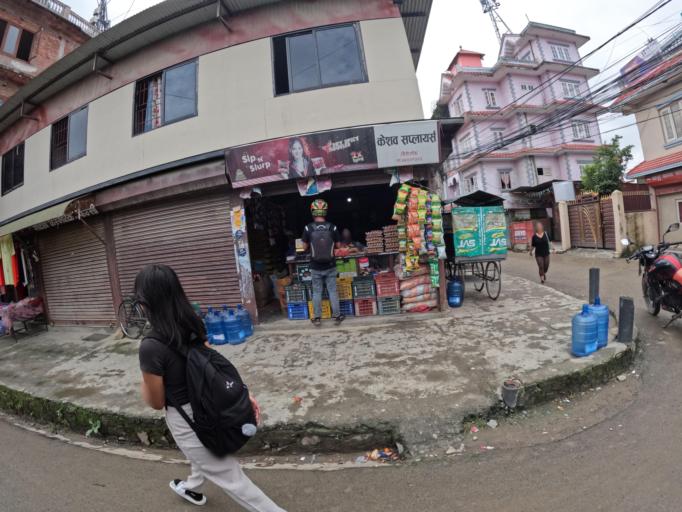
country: NP
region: Central Region
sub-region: Bagmati Zone
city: Kathmandu
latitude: 27.7474
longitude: 85.3201
